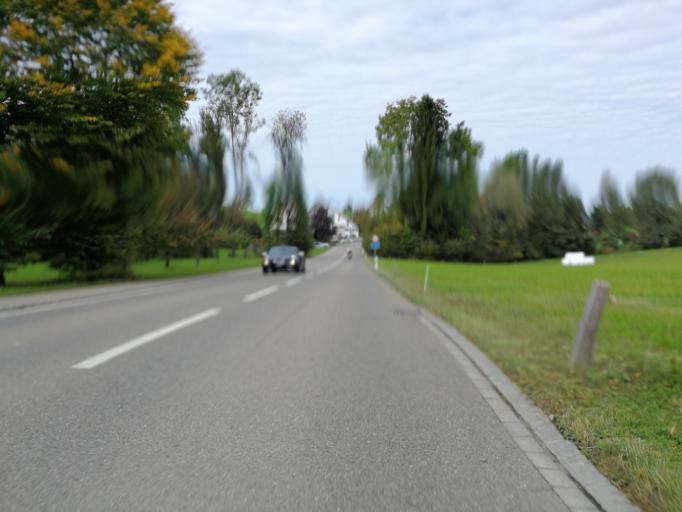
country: CH
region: Zurich
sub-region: Bezirk Meilen
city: Dorf
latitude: 47.2601
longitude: 8.7426
